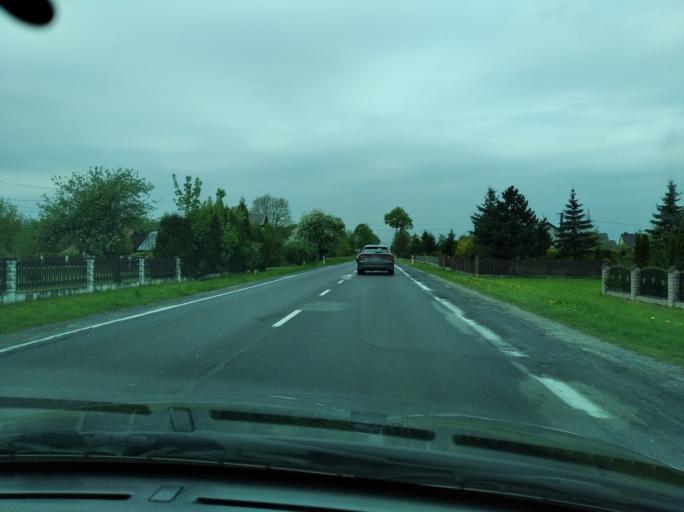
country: PL
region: Subcarpathian Voivodeship
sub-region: Powiat debicki
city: Slotowa
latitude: 49.9527
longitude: 21.3213
